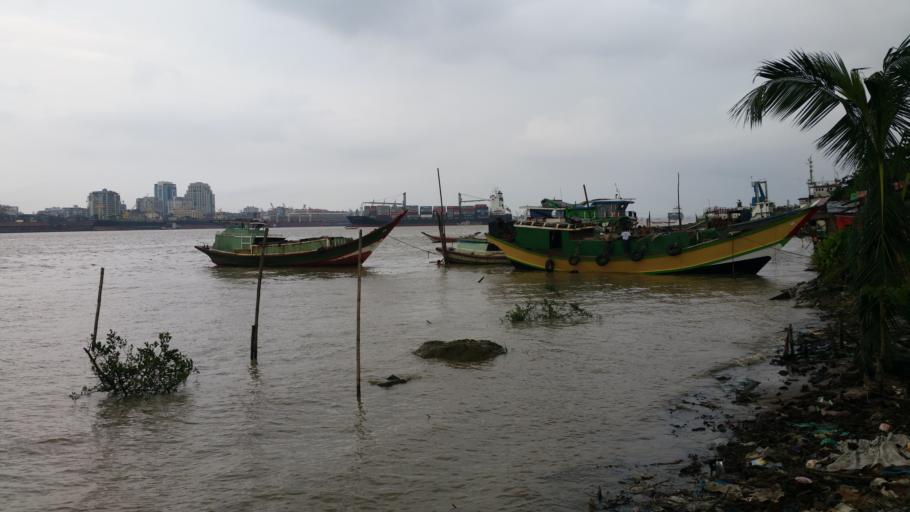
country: MM
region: Yangon
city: Yangon
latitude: 16.7654
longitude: 96.1453
